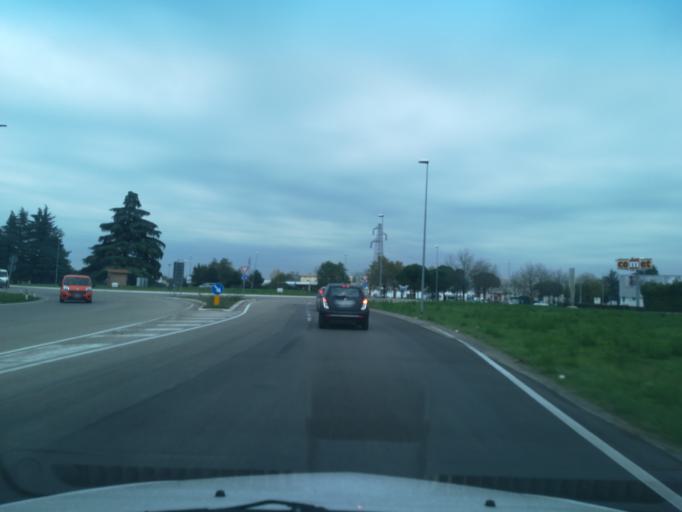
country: IT
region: Emilia-Romagna
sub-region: Provincia di Bologna
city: Imola
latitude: 44.3679
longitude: 11.7025
